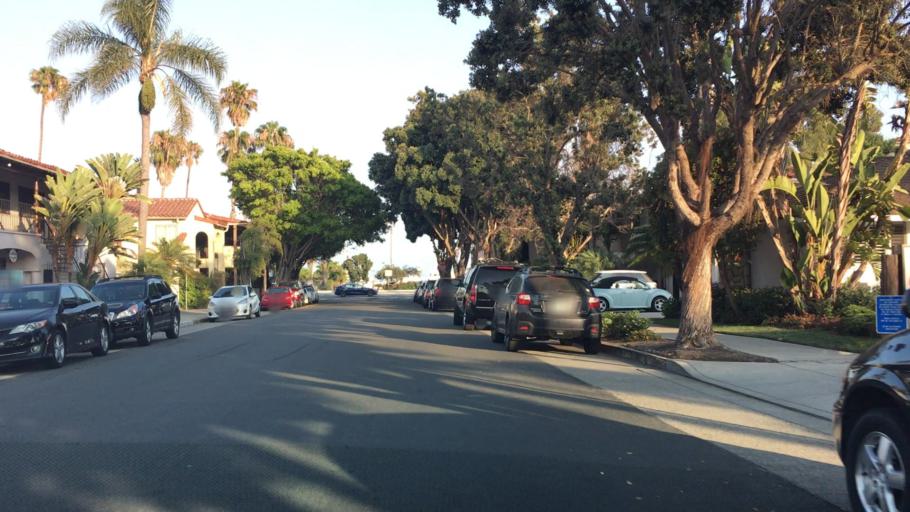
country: US
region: California
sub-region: Santa Barbara County
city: Santa Barbara
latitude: 34.4097
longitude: -119.6936
